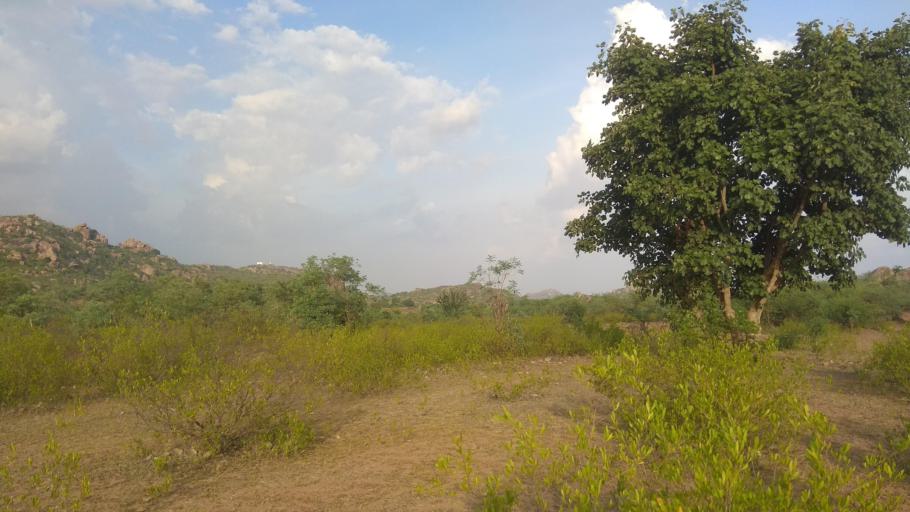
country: IN
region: Telangana
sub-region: Mahbubnagar
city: Farrukhnagar
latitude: 16.8906
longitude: 78.4832
